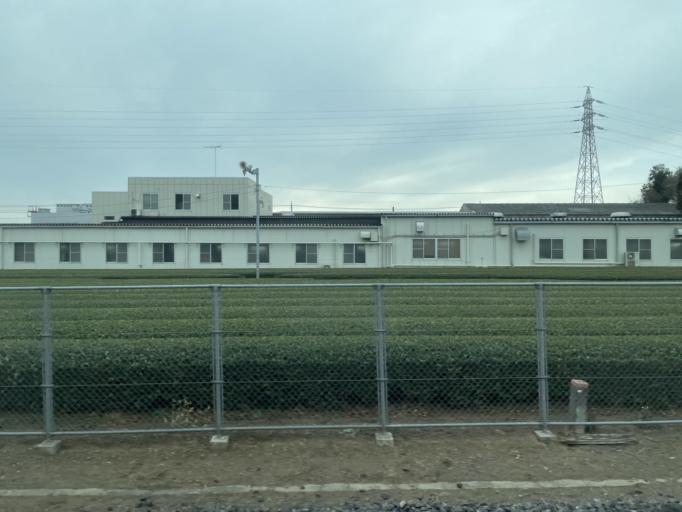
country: JP
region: Ibaraki
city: Koga
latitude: 36.1762
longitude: 139.7150
